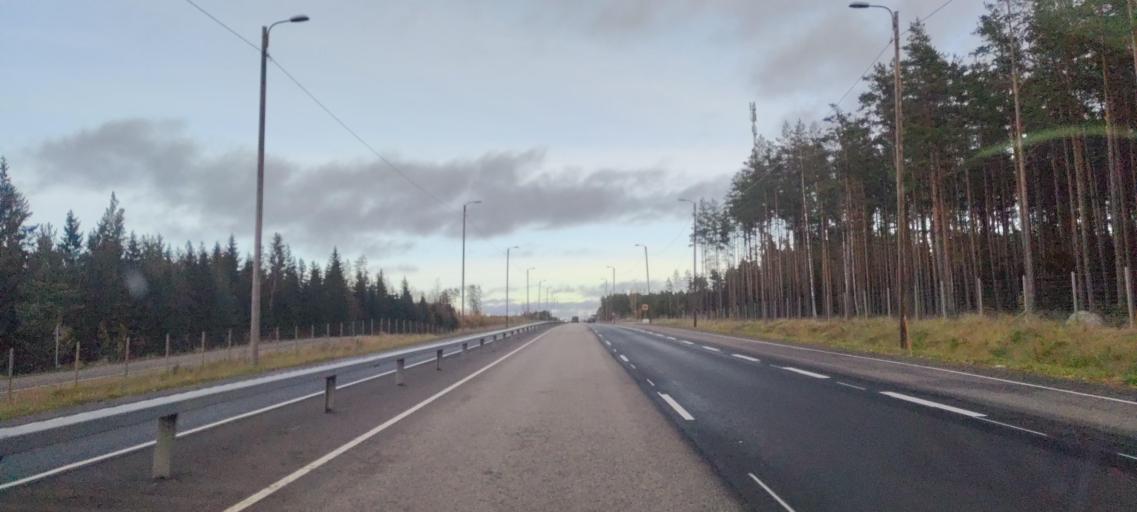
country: FI
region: Satakunta
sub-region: Pori
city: Luvia
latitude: 61.3857
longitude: 21.6741
